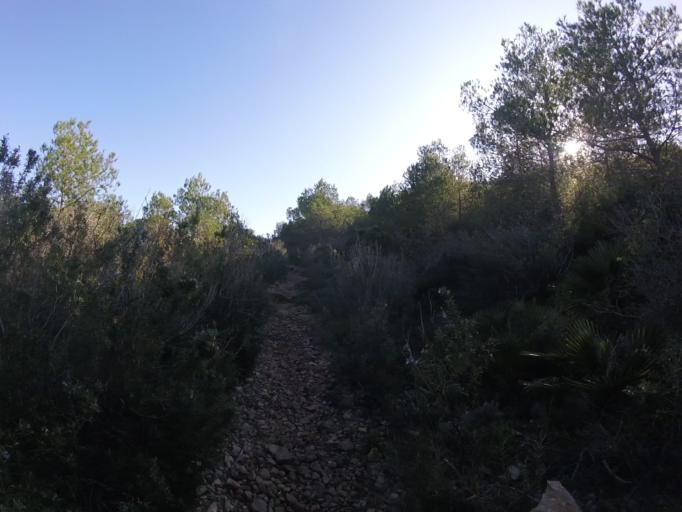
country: ES
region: Valencia
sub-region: Provincia de Castello
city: Santa Magdalena de Pulpis
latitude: 40.2998
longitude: 0.3311
